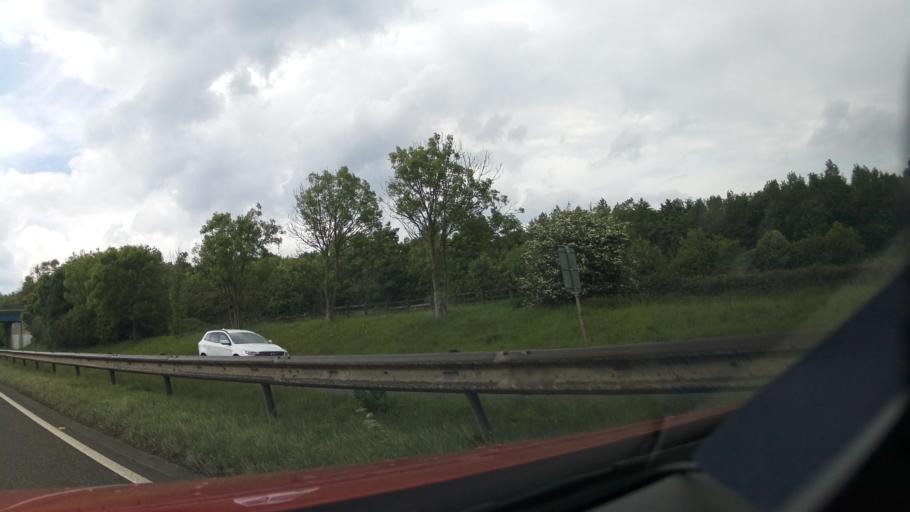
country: GB
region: England
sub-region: County Durham
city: Murton
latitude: 54.8552
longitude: -1.4150
